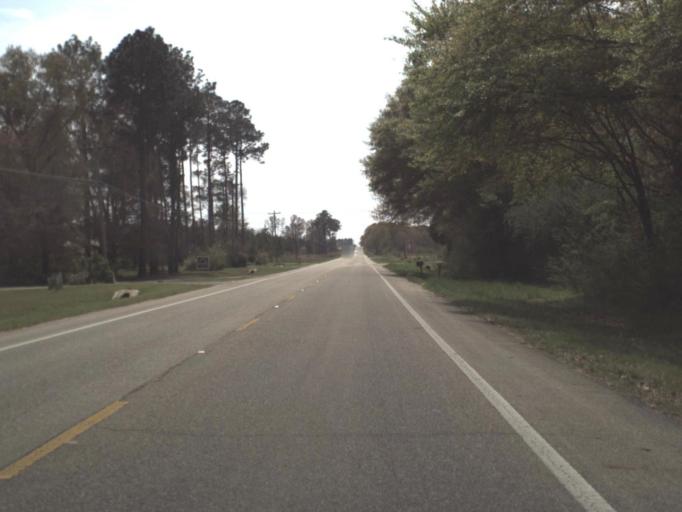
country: US
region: Florida
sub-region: Jackson County
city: Graceville
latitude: 30.9221
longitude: -85.5201
